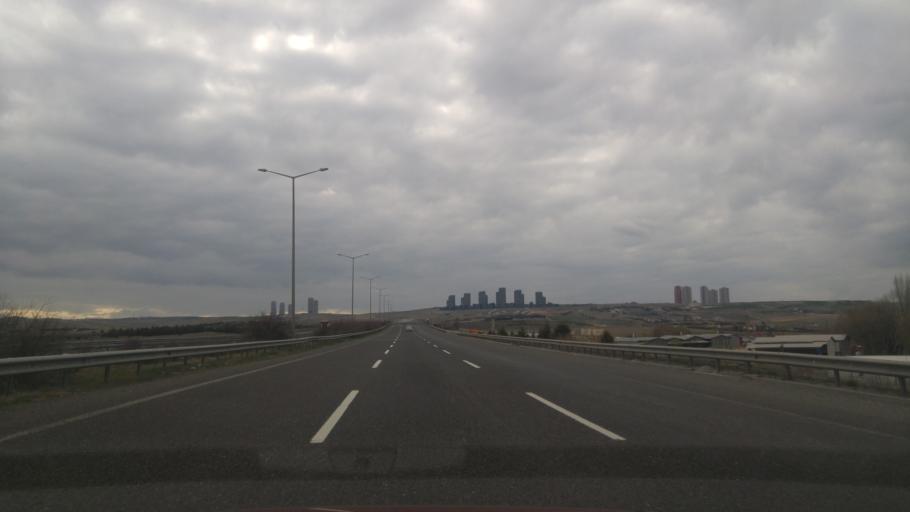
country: TR
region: Ankara
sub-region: Goelbasi
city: Golbasi
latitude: 39.7872
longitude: 32.7511
